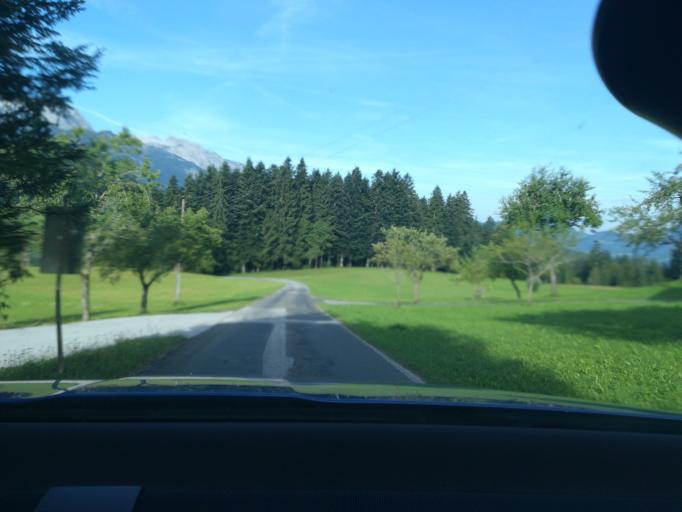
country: AT
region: Salzburg
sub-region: Politischer Bezirk Hallein
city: Abtenau
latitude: 47.5642
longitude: 13.4053
